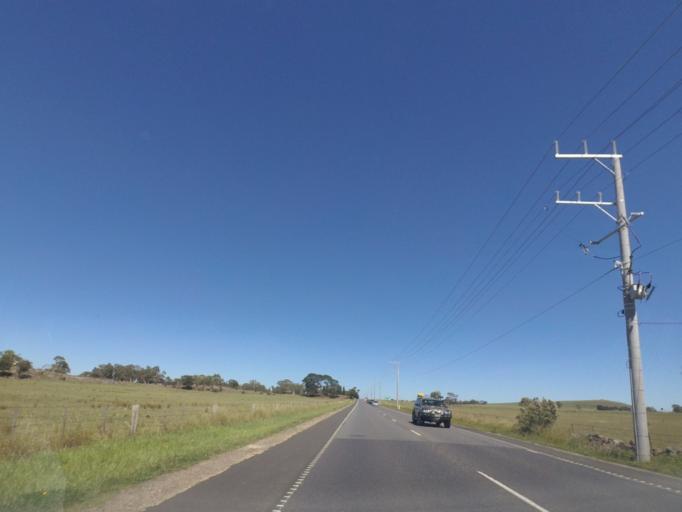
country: AU
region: Victoria
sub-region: Hume
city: Craigieburn
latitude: -37.5481
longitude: 145.0216
